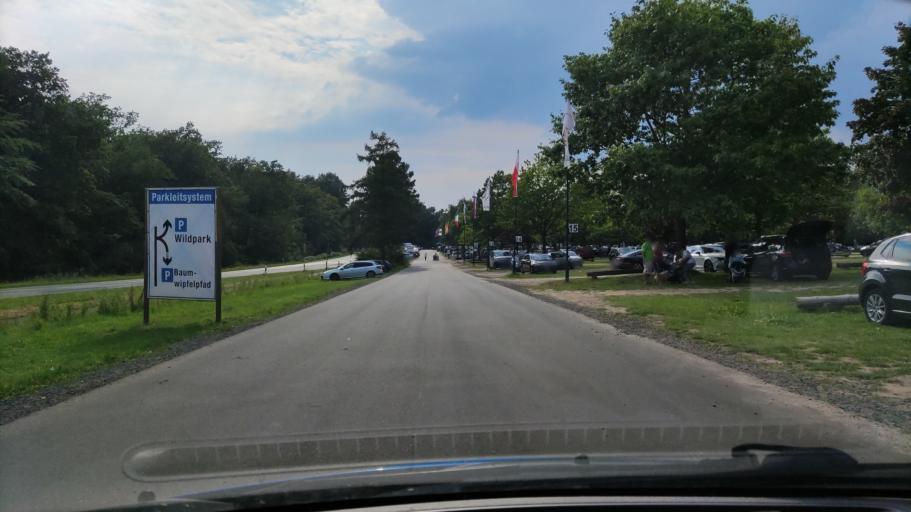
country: DE
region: Lower Saxony
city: Hanstedt
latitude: 53.2359
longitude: 10.0470
